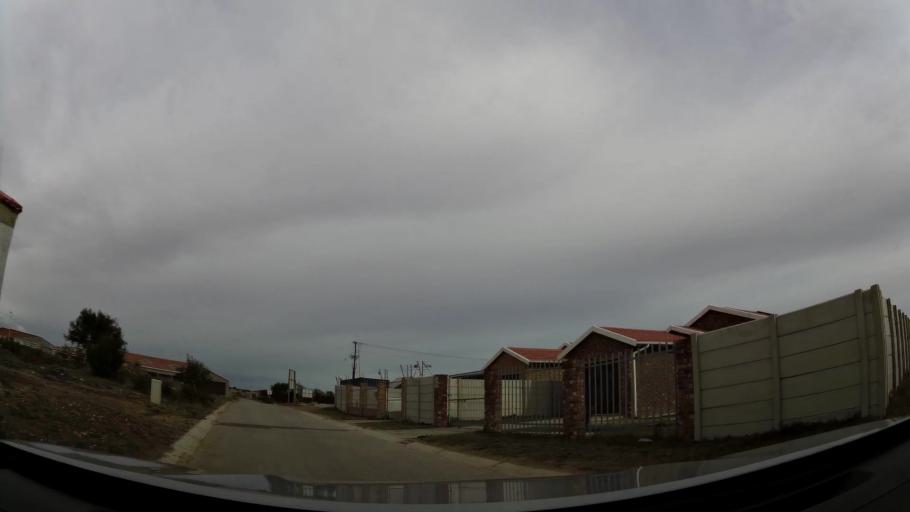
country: ZA
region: Eastern Cape
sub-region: Nelson Mandela Bay Metropolitan Municipality
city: Port Elizabeth
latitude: -33.9290
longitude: 25.5015
